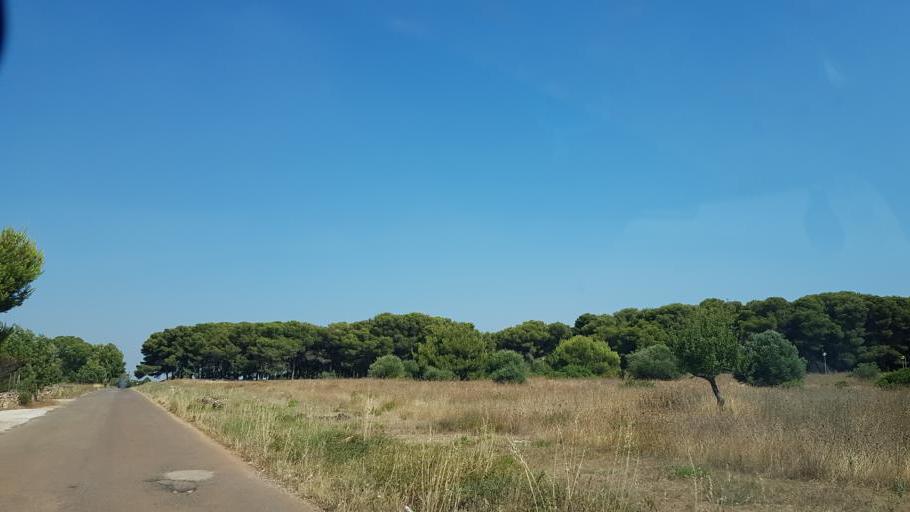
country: IT
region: Apulia
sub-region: Provincia di Lecce
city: Nardo
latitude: 40.1736
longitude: 17.9543
